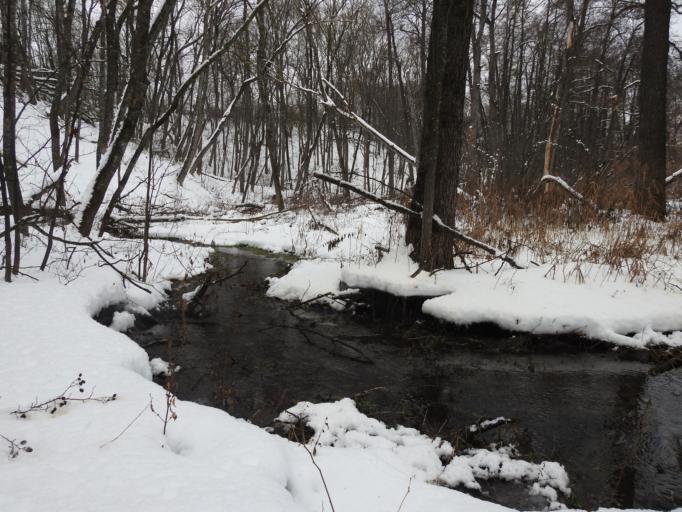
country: RU
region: Saratov
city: Tersa
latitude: 52.1059
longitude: 47.4756
